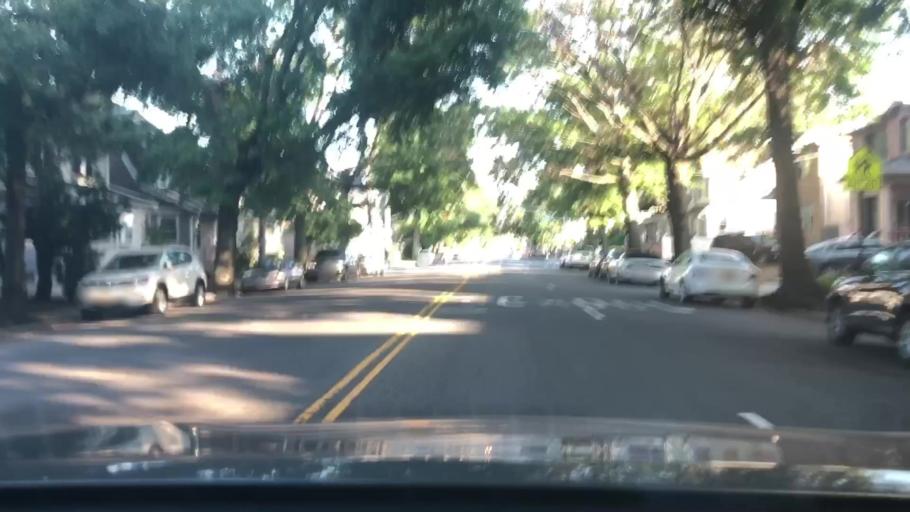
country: US
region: New York
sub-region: Nassau County
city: Bellerose Terrace
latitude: 40.7240
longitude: -73.7386
